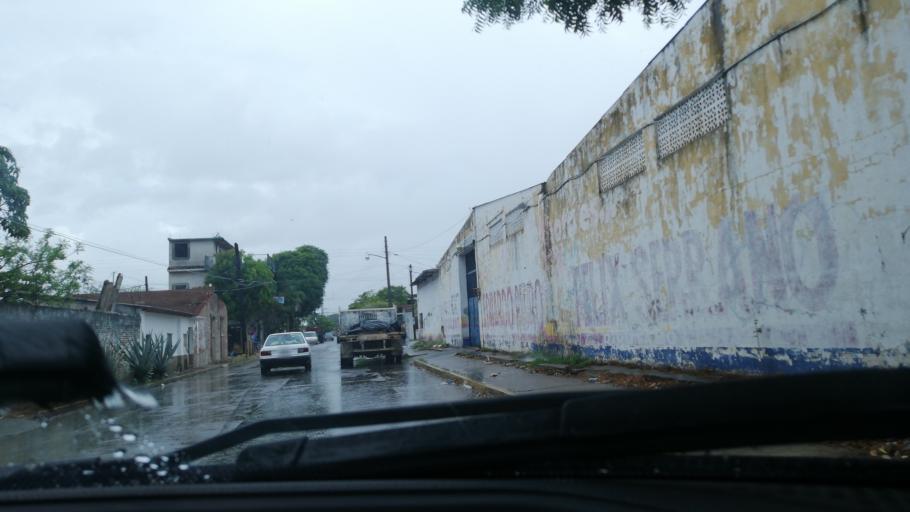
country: MX
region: Oaxaca
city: San Jeronimo Ixtepec
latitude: 16.5544
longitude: -95.0983
